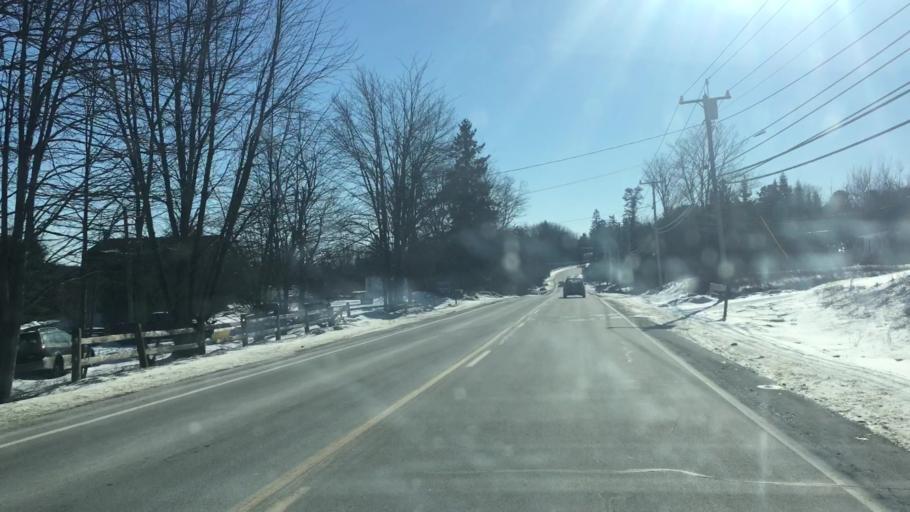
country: US
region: Maine
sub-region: Hancock County
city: Ellsworth
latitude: 44.5238
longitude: -68.4315
